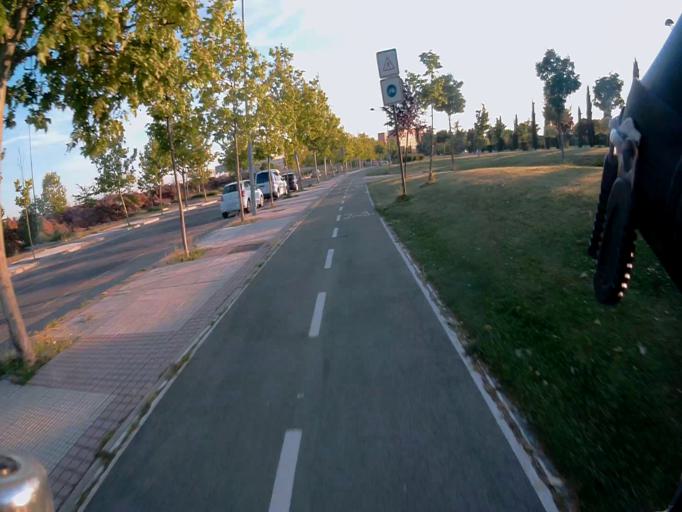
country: ES
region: Madrid
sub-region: Provincia de Madrid
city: Alcorcon
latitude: 40.3354
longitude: -3.8222
